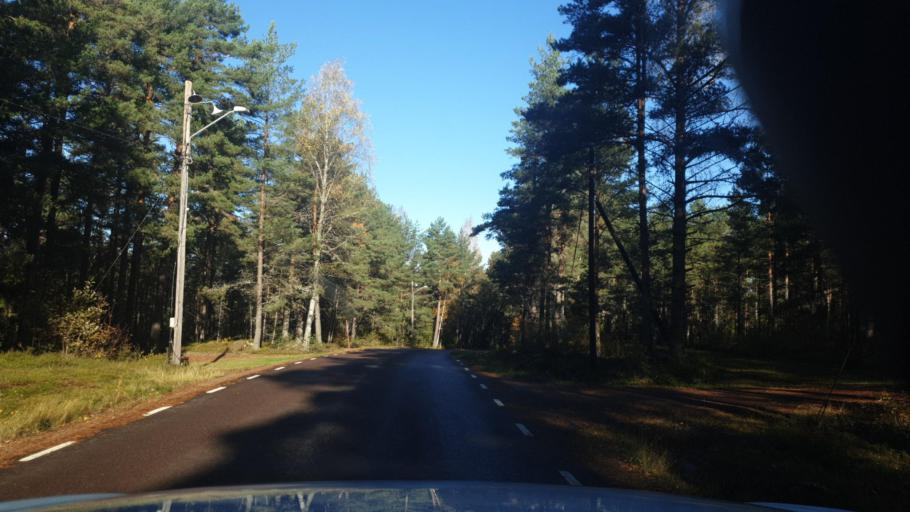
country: SE
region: Vaermland
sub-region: Arvika Kommun
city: Arvika
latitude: 59.5348
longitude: 12.7416
